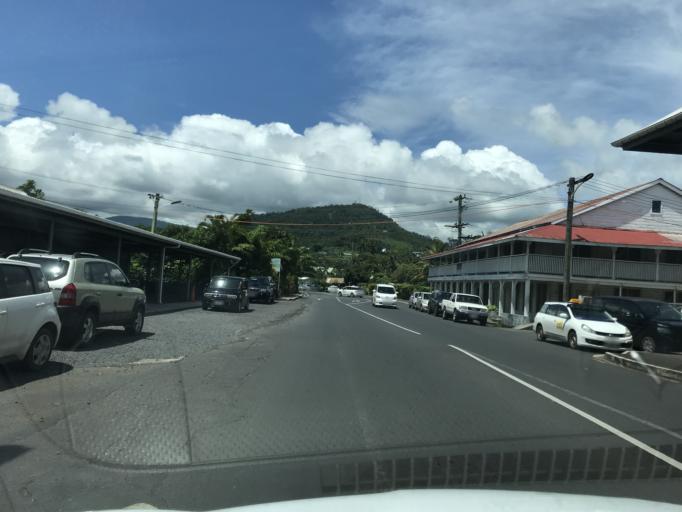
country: WS
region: Tuamasaga
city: Apia
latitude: -13.8335
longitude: -171.7637
